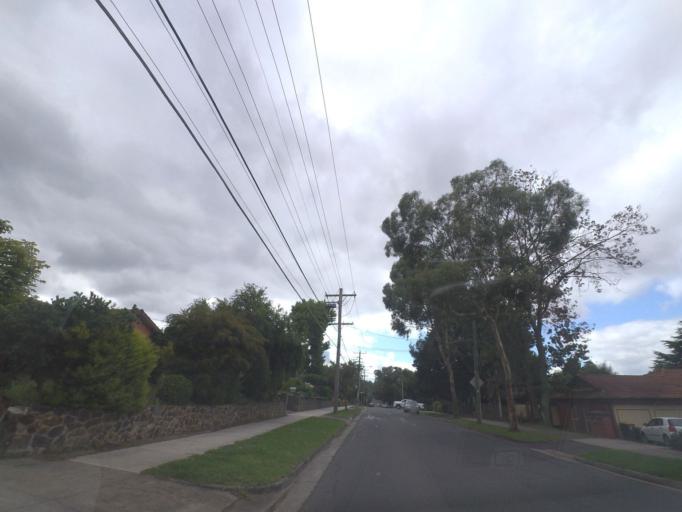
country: AU
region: Victoria
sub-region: Whitehorse
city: Vermont
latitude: -37.8304
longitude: 145.2087
